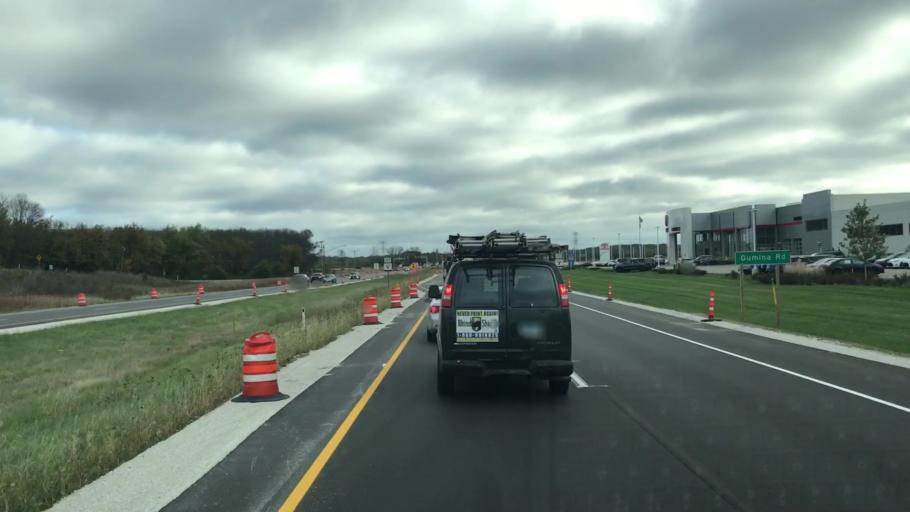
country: US
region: Wisconsin
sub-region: Waukesha County
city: Lannon
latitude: 43.0854
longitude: -88.1707
